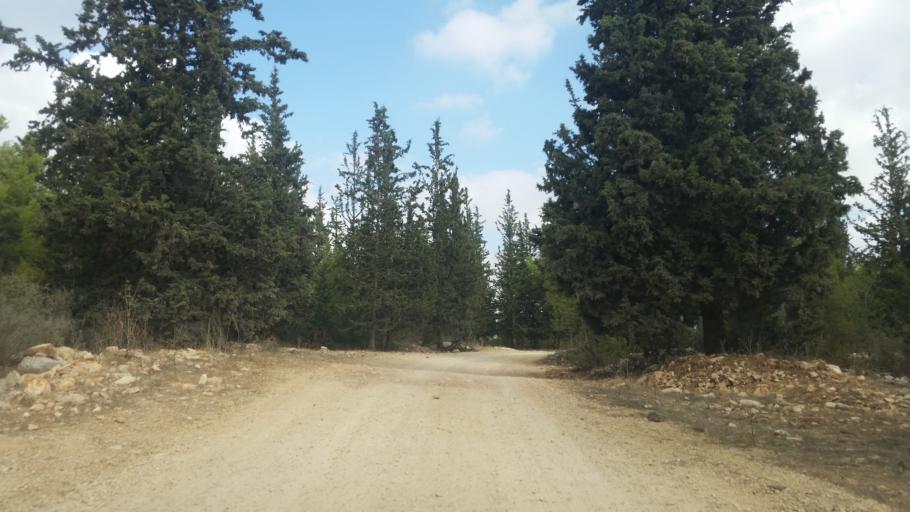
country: IL
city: Hashmonaim
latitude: 31.9219
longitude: 35.0104
